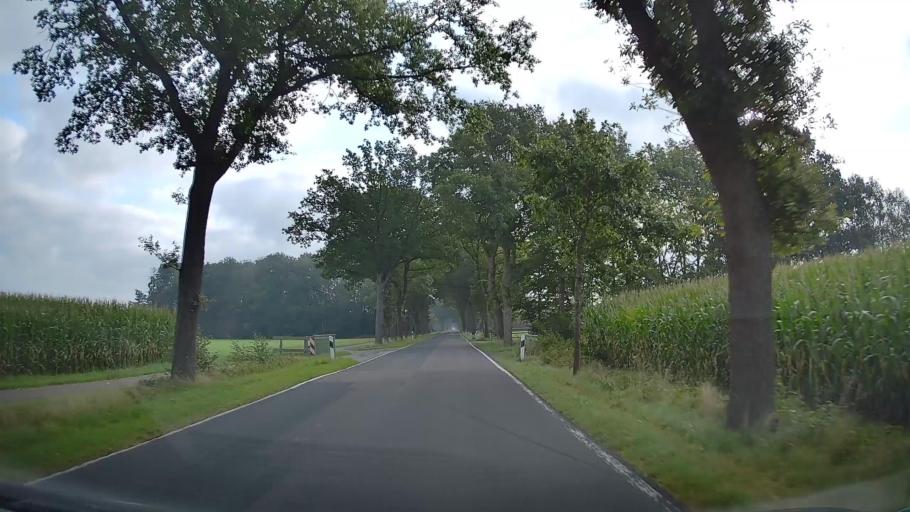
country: DE
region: Lower Saxony
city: Wardenburg
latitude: 53.0043
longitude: 8.1527
